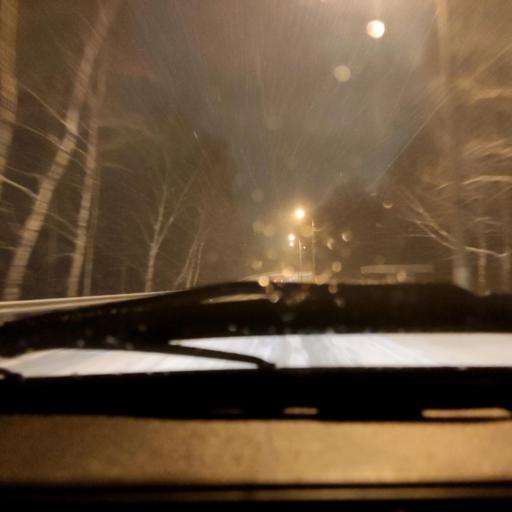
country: RU
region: Bashkortostan
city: Ufa
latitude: 54.8541
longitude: 56.0734
